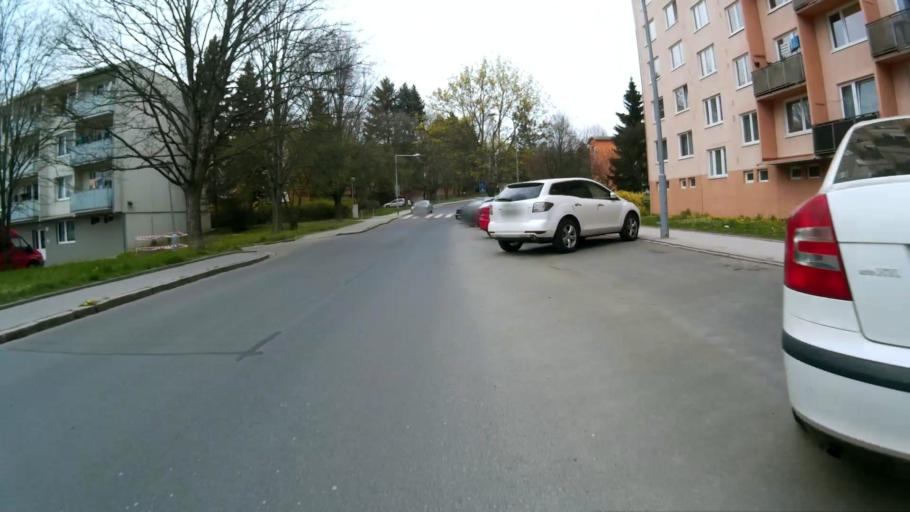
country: CZ
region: South Moravian
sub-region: Mesto Brno
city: Mokra Hora
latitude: 49.2200
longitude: 16.5562
